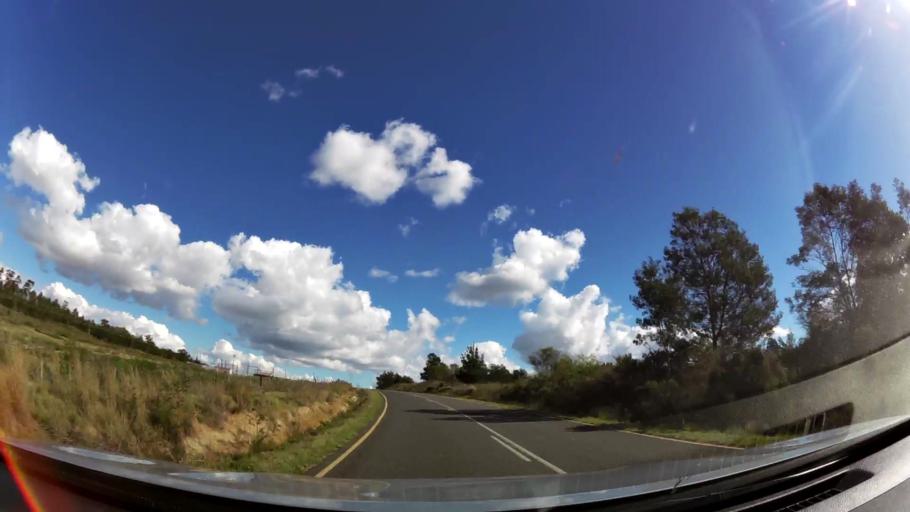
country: ZA
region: Western Cape
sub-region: Overberg District Municipality
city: Swellendam
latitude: -34.0243
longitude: 20.4291
